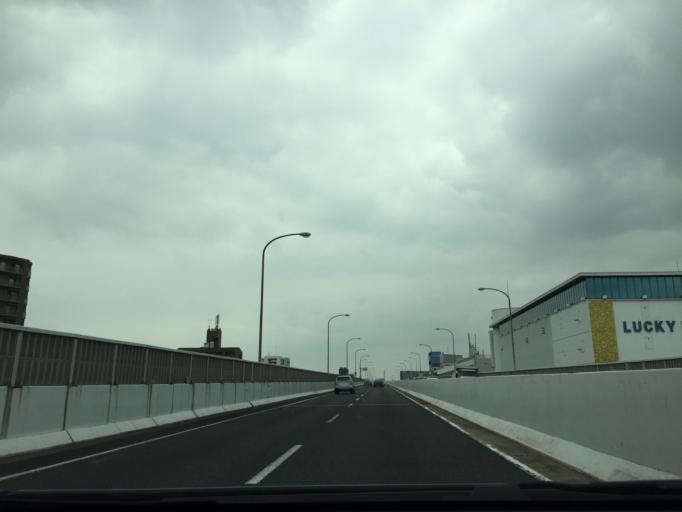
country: JP
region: Aichi
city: Nagoya-shi
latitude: 35.1135
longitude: 136.9221
